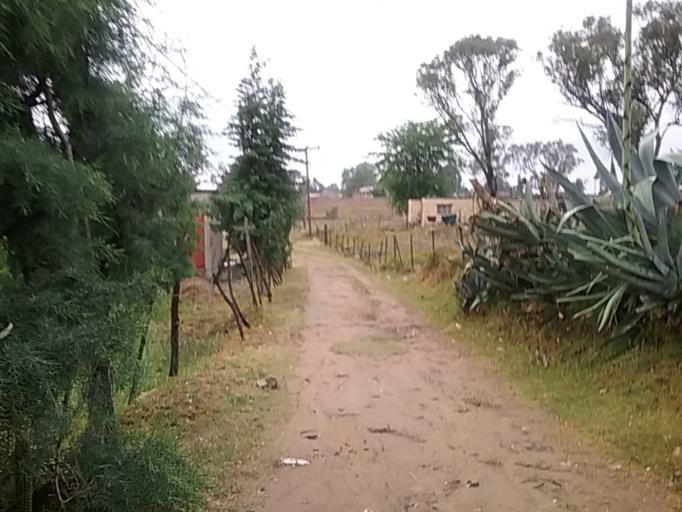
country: LS
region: Berea
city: Teyateyaneng
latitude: -29.1410
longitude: 27.7384
